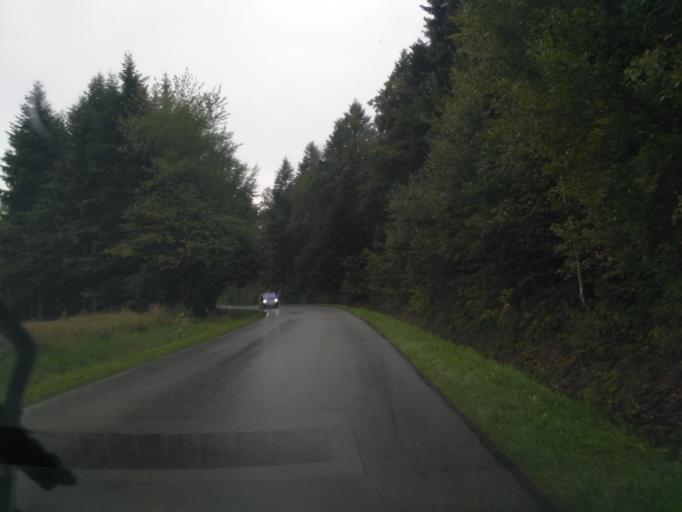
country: PL
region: Subcarpathian Voivodeship
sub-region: Powiat ropczycko-sedziszowski
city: Zagorzyce
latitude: 49.9553
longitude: 21.6944
